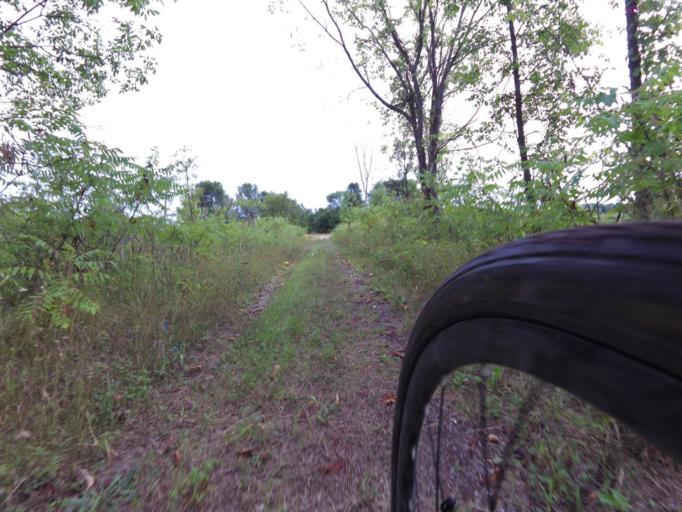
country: CA
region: Ontario
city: Perth
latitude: 44.6236
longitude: -76.2454
